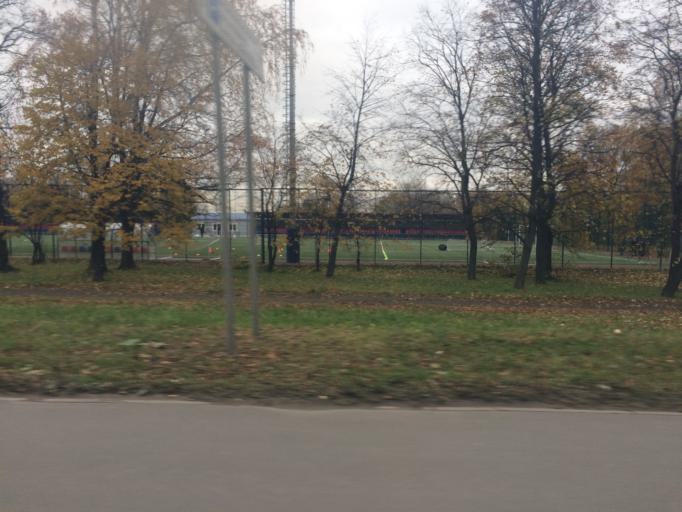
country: RU
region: Leningrad
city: Rybatskoye
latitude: 59.8490
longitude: 30.4828
